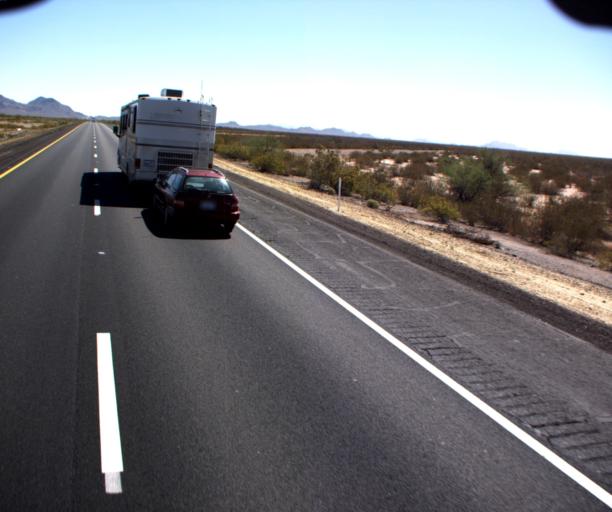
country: US
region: Arizona
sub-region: La Paz County
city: Salome
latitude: 33.6239
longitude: -113.7216
